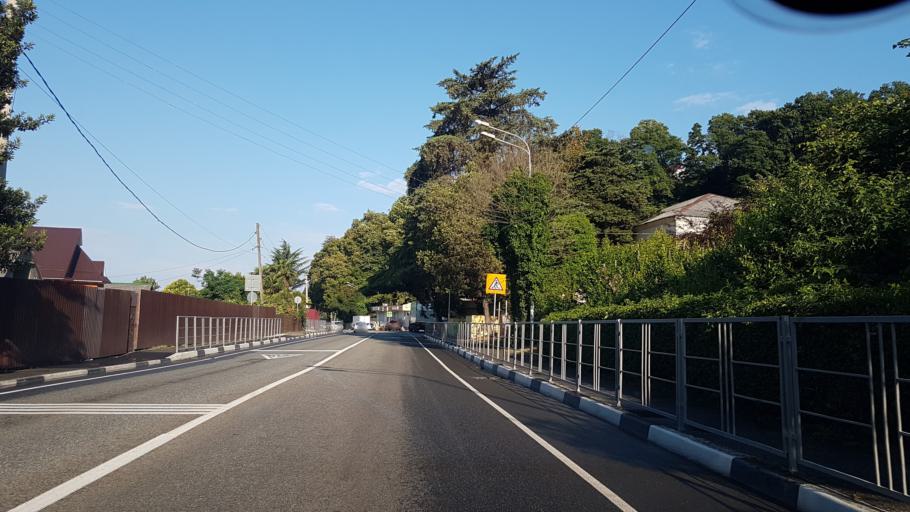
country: RU
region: Krasnodarskiy
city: Vardane
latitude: 43.7987
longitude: 39.4668
